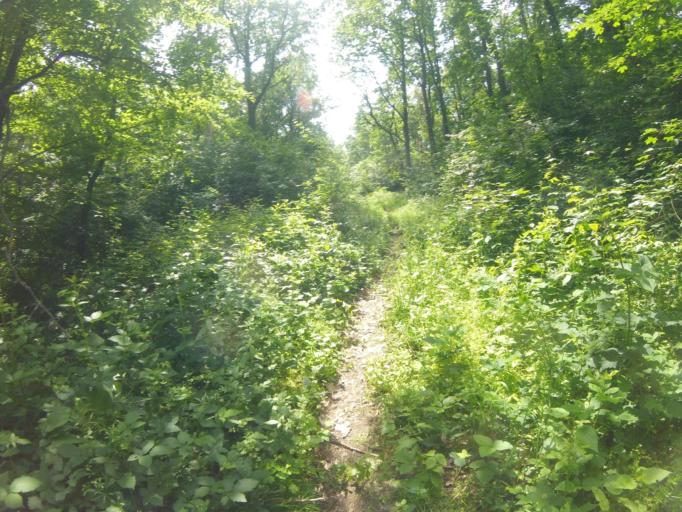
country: HU
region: Zala
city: Cserszegtomaj
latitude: 46.9061
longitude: 17.1932
